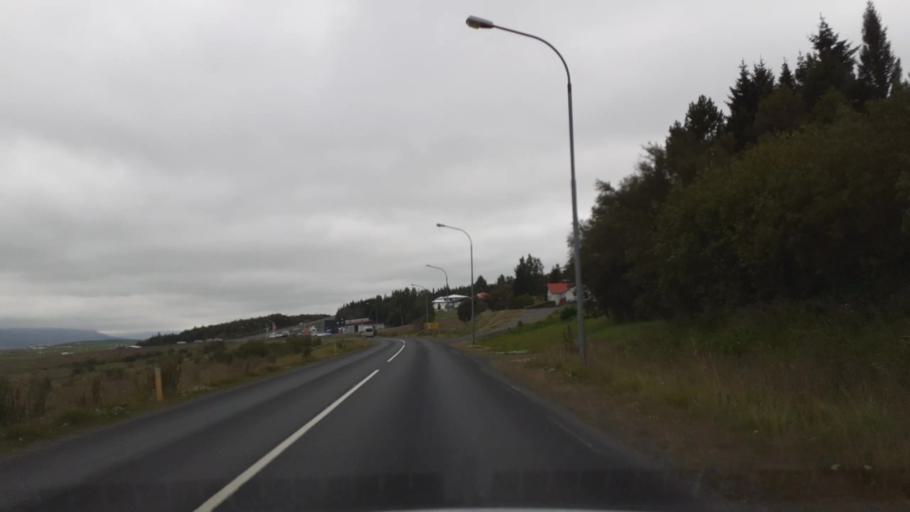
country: IS
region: Northwest
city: Saudarkrokur
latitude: 65.5564
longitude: -19.4507
